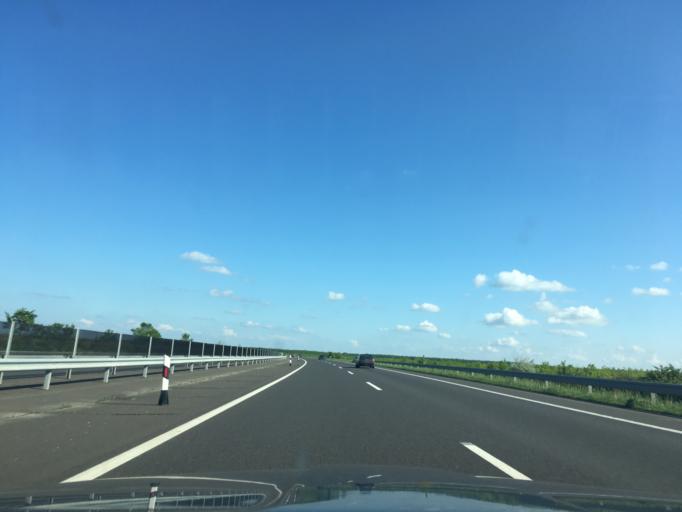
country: HU
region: Hajdu-Bihar
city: Polgar
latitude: 47.8150
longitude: 21.1555
